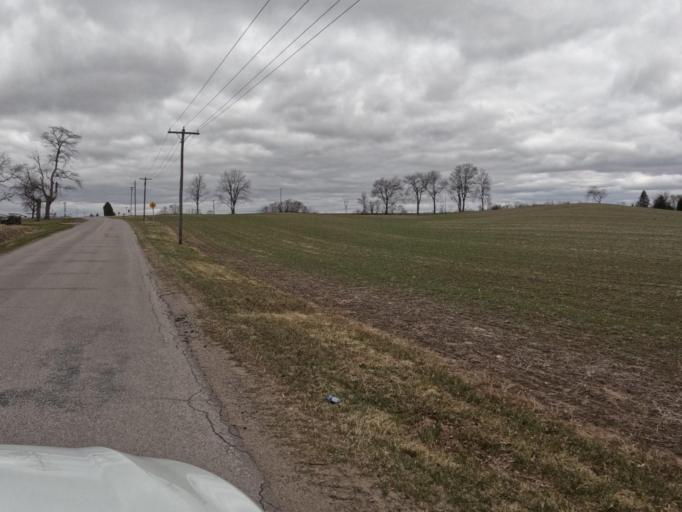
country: CA
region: Ontario
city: Norfolk County
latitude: 42.9554
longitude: -80.3943
